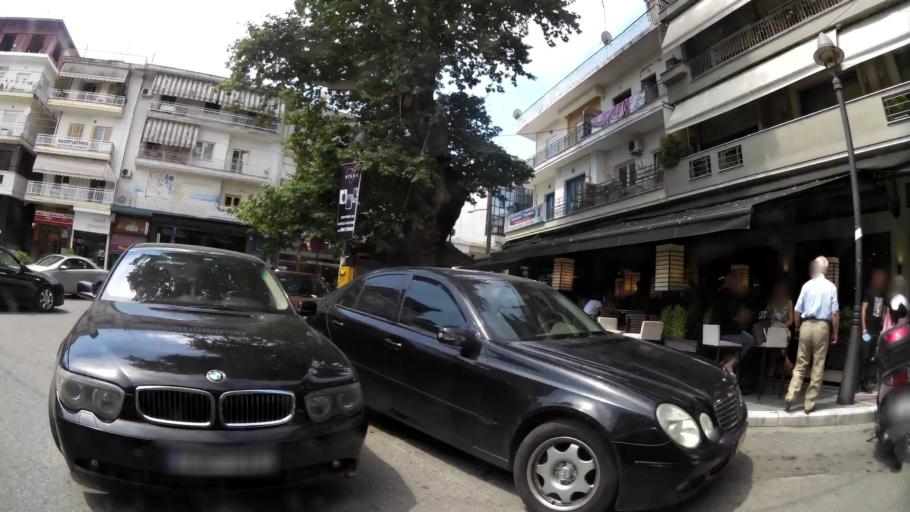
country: GR
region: Central Macedonia
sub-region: Nomos Pierias
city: Katerini
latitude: 40.2719
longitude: 22.5042
